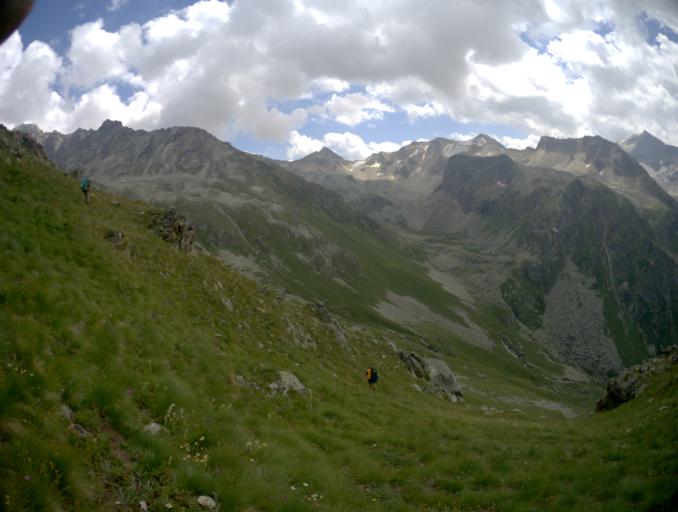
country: RU
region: Karachayevo-Cherkesiya
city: Uchkulan
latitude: 43.2956
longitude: 42.0736
